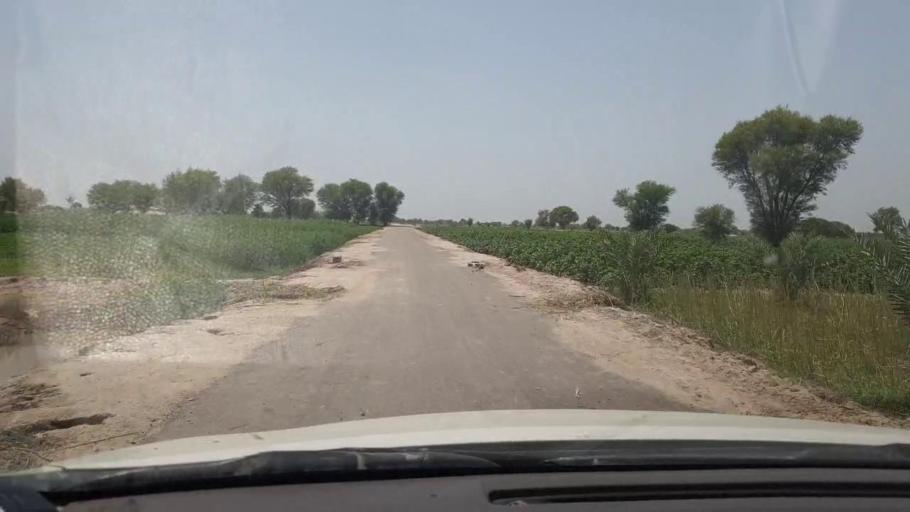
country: PK
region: Sindh
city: Rohri
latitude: 27.5207
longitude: 69.1803
